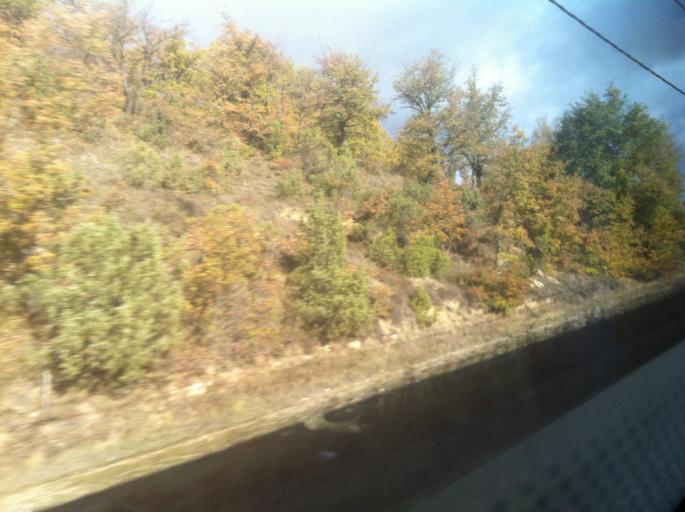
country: ES
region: Basque Country
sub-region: Provincia de Alava
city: Arminon
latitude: 42.7396
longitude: -2.8722
